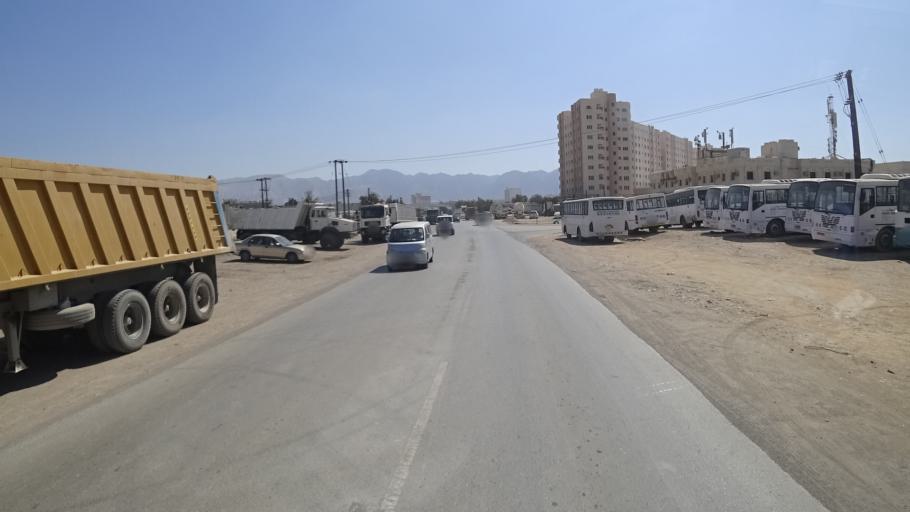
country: OM
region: Muhafazat Masqat
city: Bawshar
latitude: 23.5778
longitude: 58.3658
